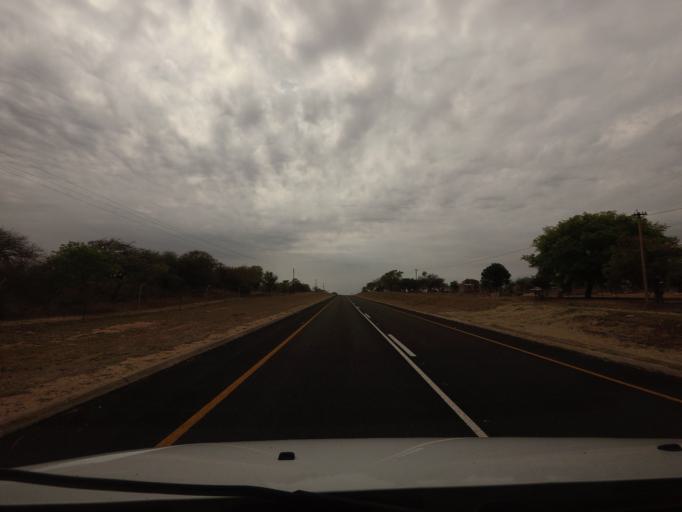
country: ZA
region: Limpopo
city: Thulamahashi
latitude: -24.5620
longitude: 31.1521
